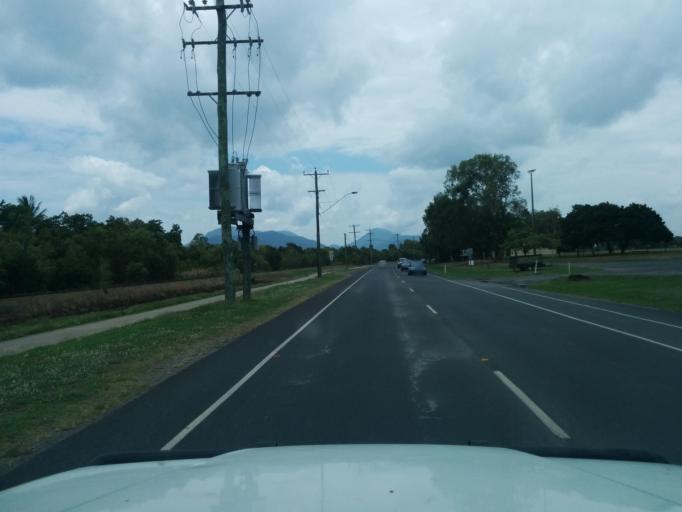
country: AU
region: Queensland
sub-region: Cairns
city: Cairns
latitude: -16.8863
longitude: 145.7485
